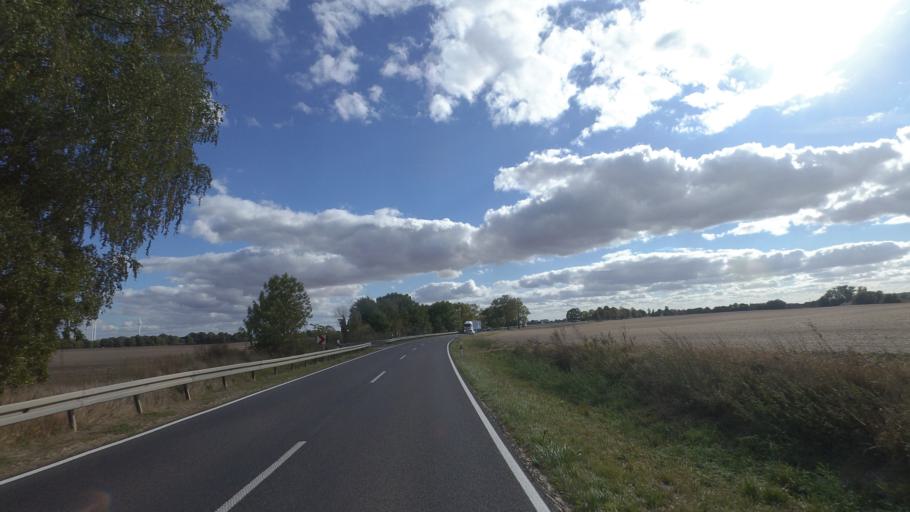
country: DE
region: Brandenburg
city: Gransee
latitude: 53.0455
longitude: 13.1981
